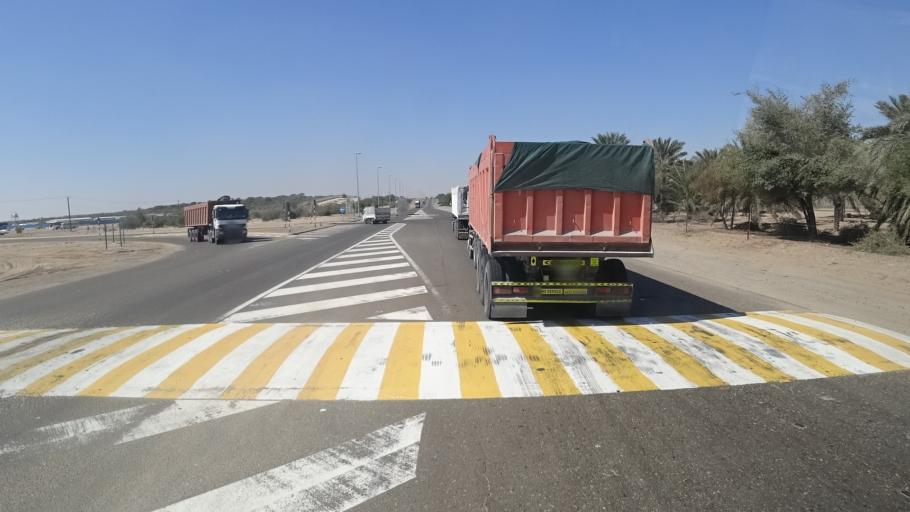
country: AE
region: Abu Dhabi
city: Abu Dhabi
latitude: 24.2244
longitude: 54.7534
